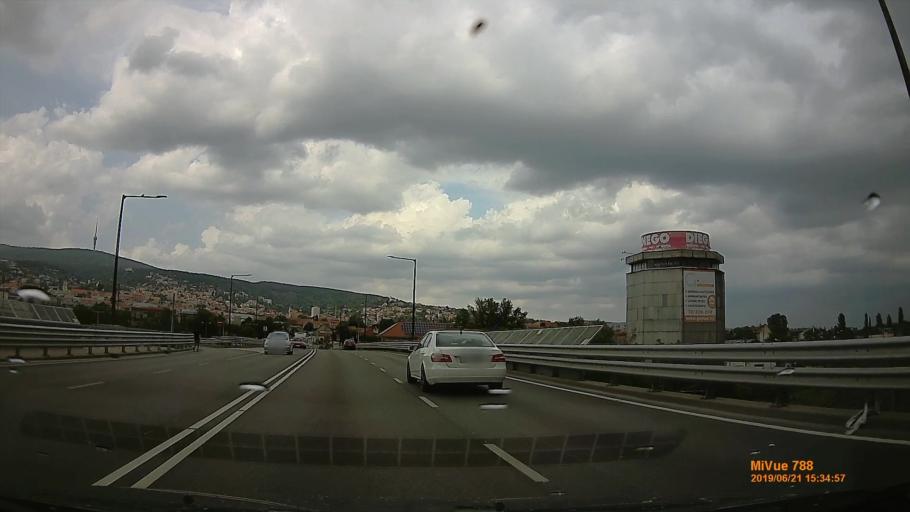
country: HU
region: Baranya
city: Pecs
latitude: 46.0679
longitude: 18.2328
